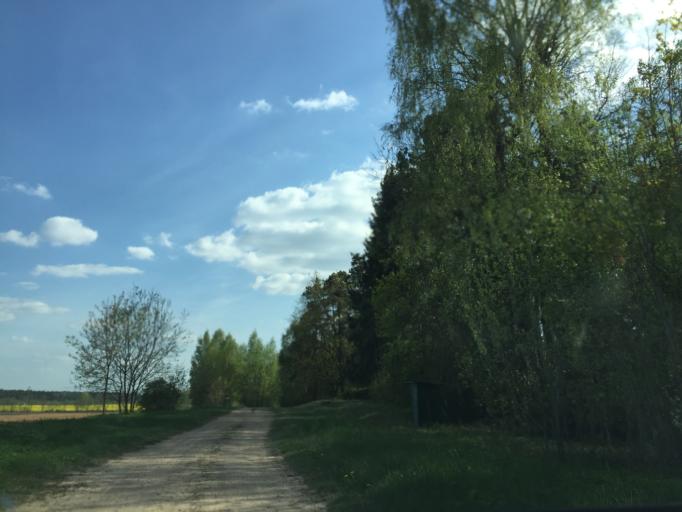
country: LV
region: Vecumnieki
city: Vecumnieki
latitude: 56.5370
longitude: 24.4184
